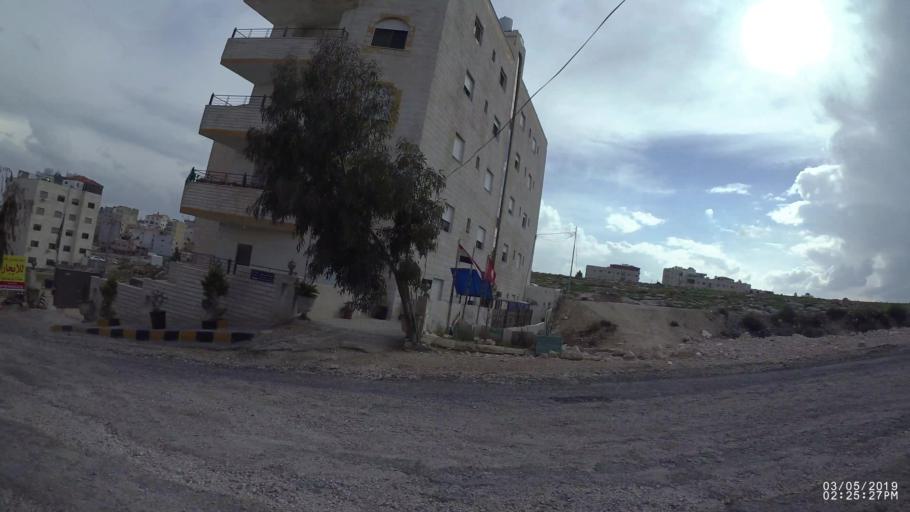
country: JO
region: Amman
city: Amman
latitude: 32.0164
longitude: 35.9421
